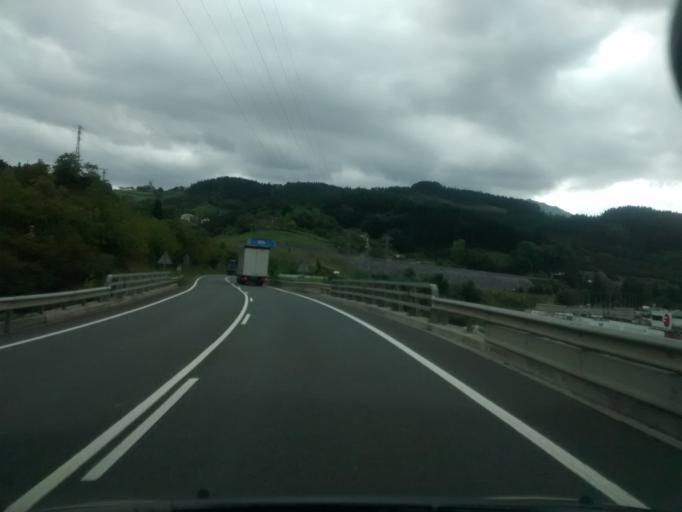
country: ES
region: Basque Country
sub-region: Provincia de Guipuzcoa
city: Arrasate / Mondragon
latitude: 43.0568
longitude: -2.4918
